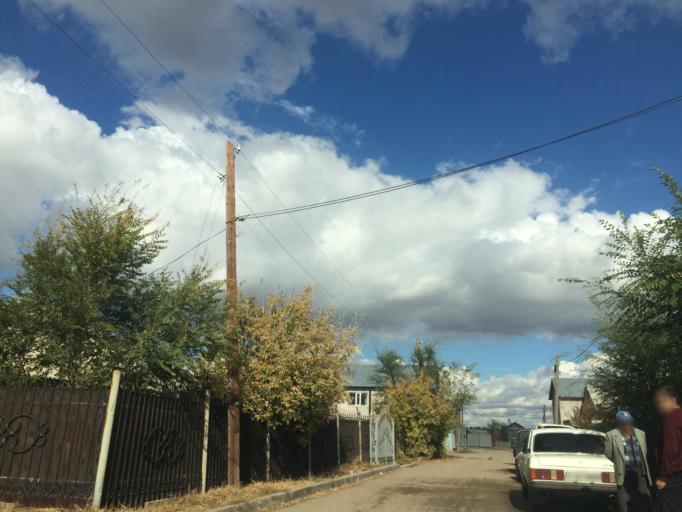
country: KZ
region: Astana Qalasy
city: Astana
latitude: 51.1859
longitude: 71.3841
